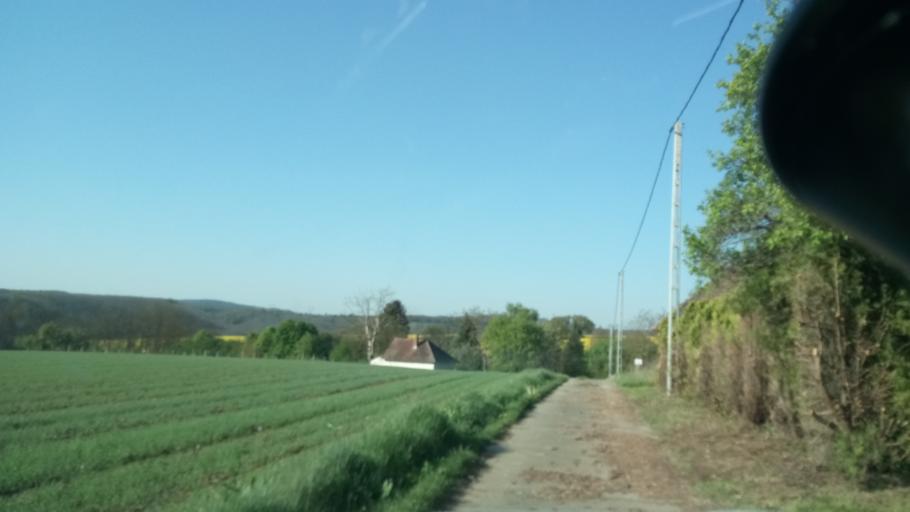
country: HU
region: Zala
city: Sarmellek
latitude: 46.7007
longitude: 17.0975
